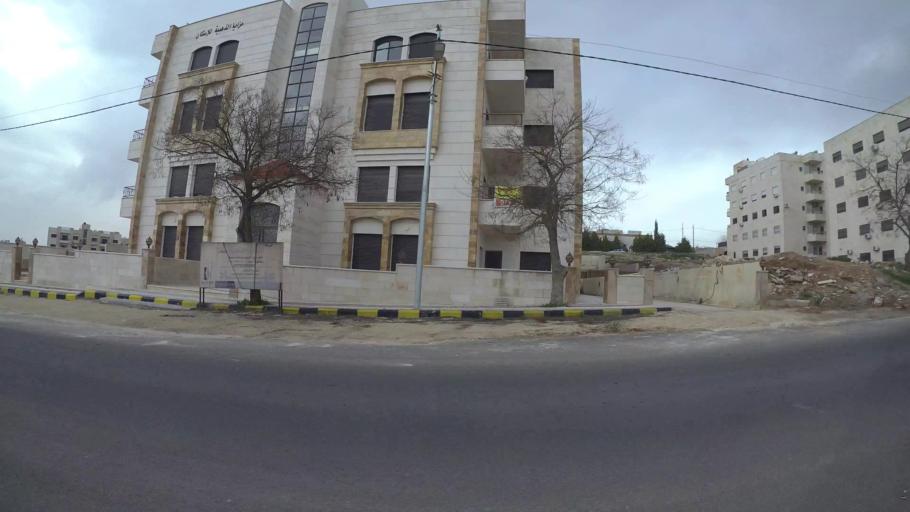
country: JO
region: Amman
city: Umm as Summaq
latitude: 31.9065
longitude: 35.8366
